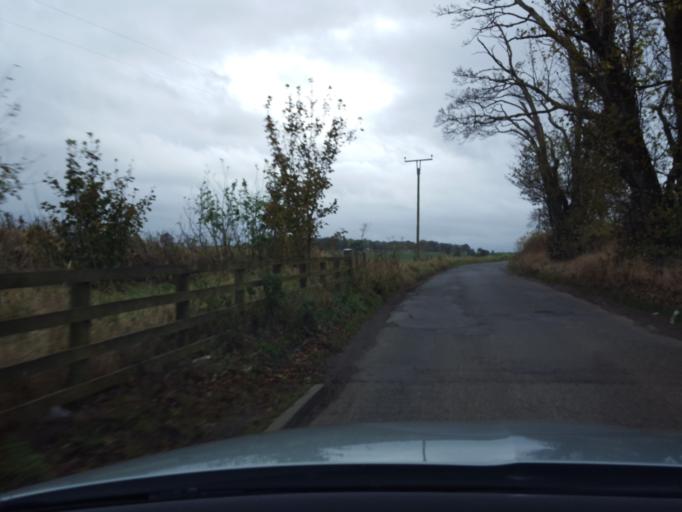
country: GB
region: Scotland
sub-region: Edinburgh
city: Newbridge
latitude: 55.9159
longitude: -3.4101
